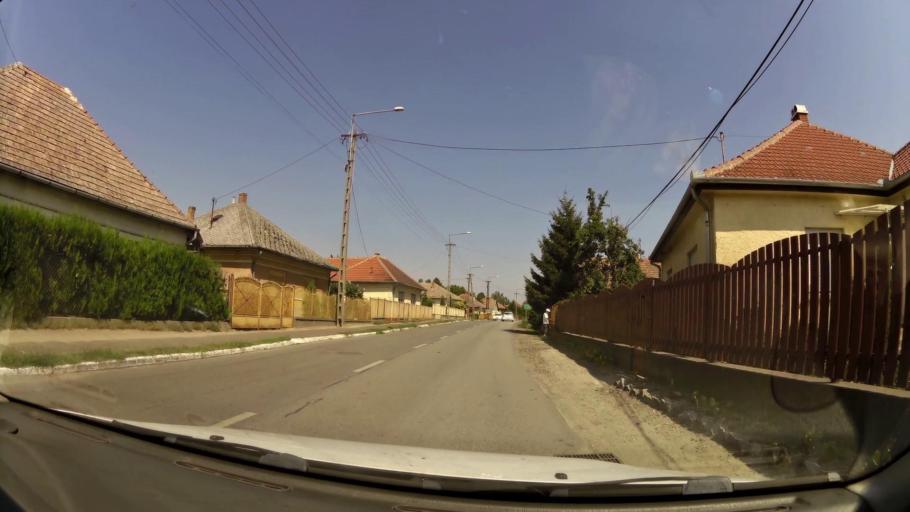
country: HU
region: Pest
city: Tapiobicske
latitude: 47.3644
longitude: 19.6885
